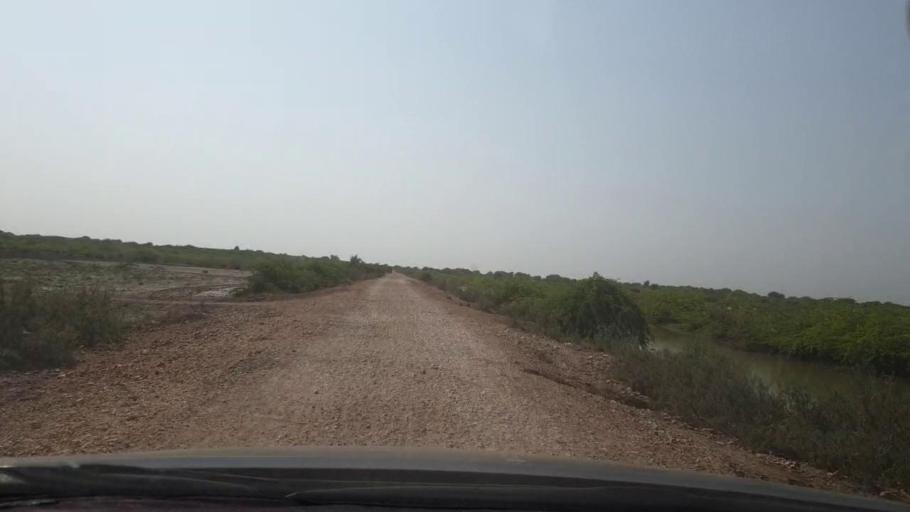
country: PK
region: Sindh
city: Naukot
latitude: 24.7959
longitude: 69.2314
